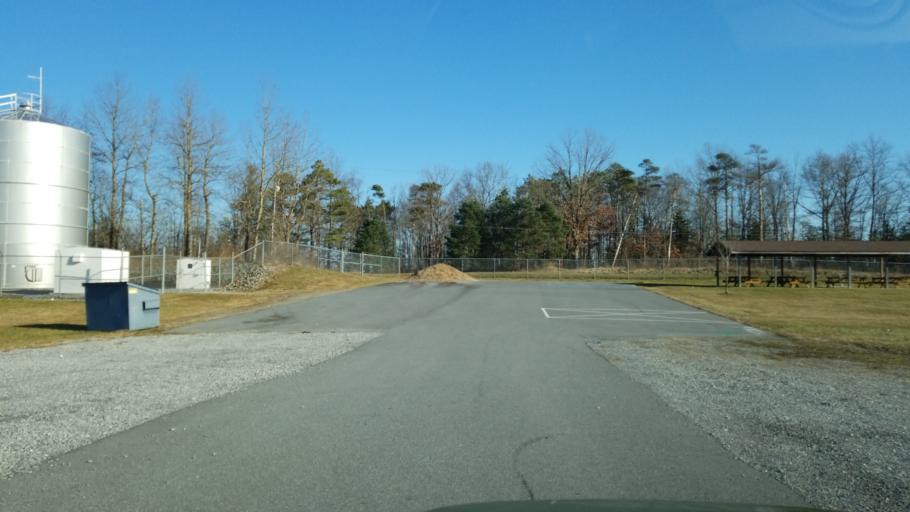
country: US
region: Pennsylvania
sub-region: Clearfield County
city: Clearfield
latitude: 41.0100
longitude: -78.4221
